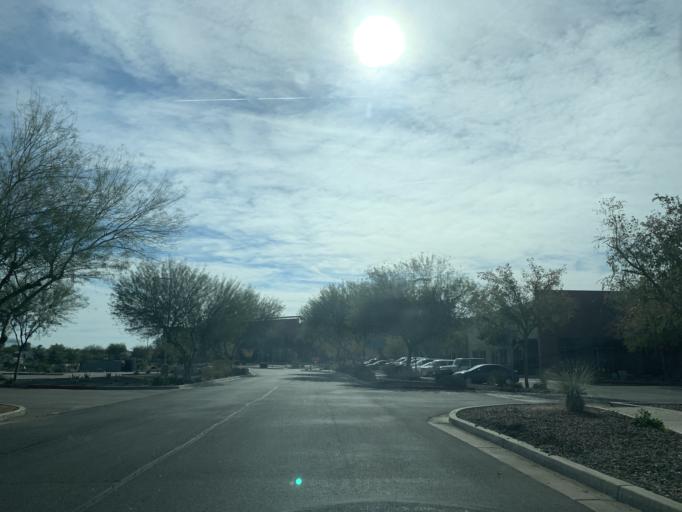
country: US
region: Arizona
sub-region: Maricopa County
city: Chandler
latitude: 33.2763
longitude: -111.7839
